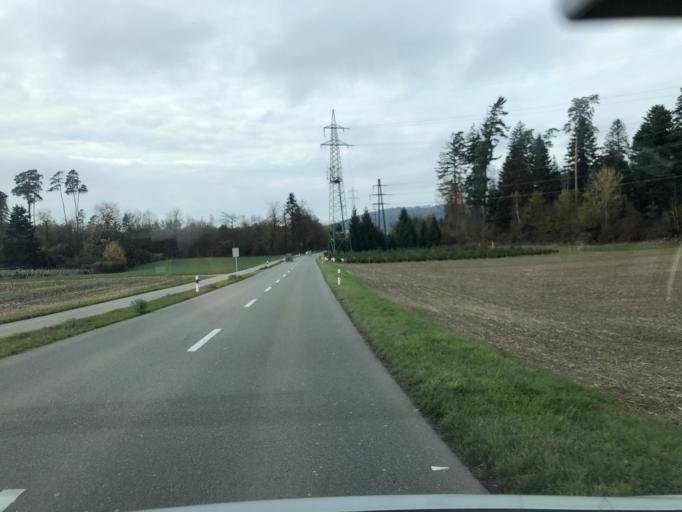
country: CH
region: Aargau
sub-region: Bezirk Baden
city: Mellingen
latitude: 47.4443
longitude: 8.2797
